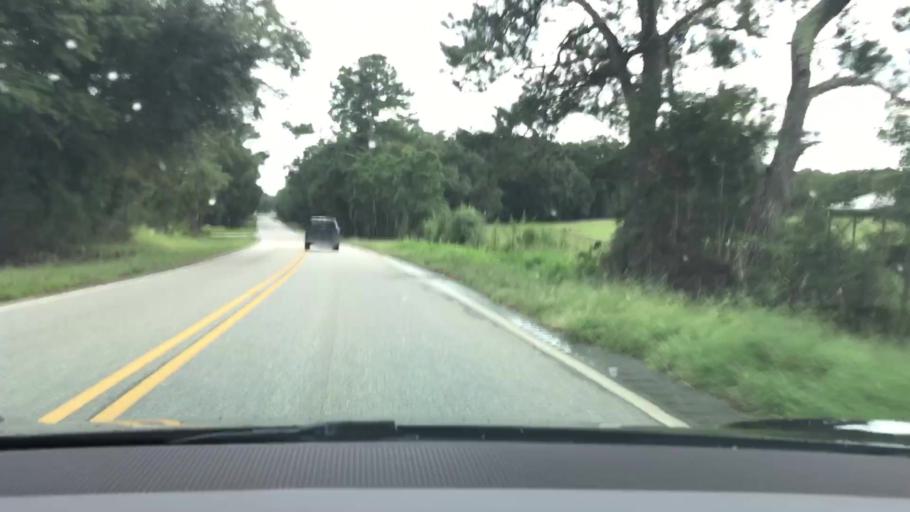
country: US
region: Alabama
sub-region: Geneva County
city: Samson
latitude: 30.9999
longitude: -86.1322
